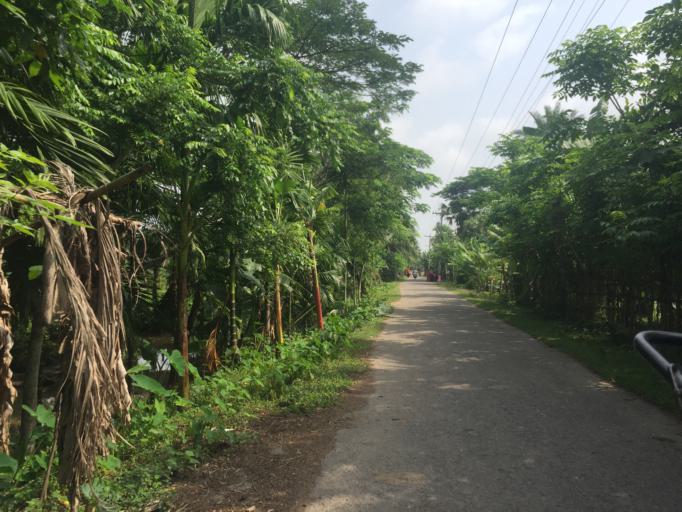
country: BD
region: Barisal
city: Mathba
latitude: 22.2324
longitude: 89.9157
